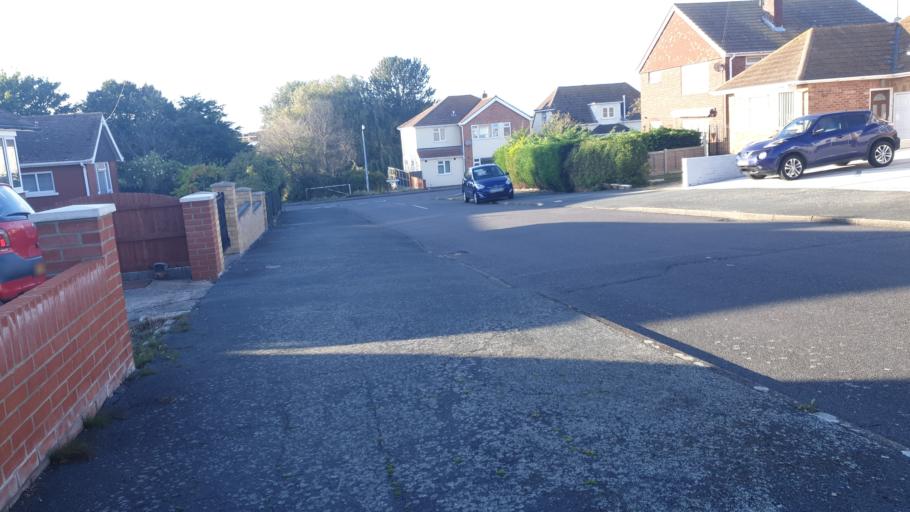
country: GB
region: England
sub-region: Essex
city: Clacton-on-Sea
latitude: 51.8050
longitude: 1.1796
